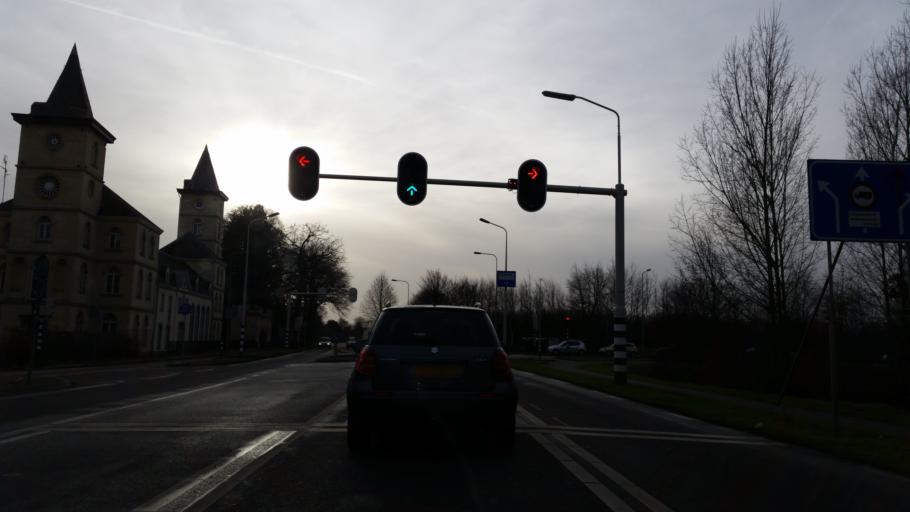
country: NL
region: Limburg
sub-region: Gemeente Meerssen
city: Meerssen
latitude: 50.8721
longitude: 5.7220
